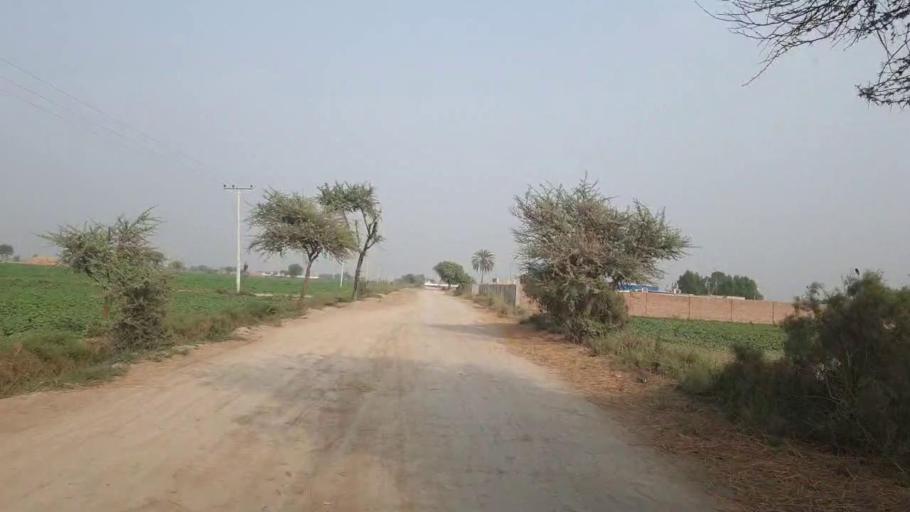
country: PK
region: Sindh
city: Mirpur Batoro
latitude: 24.5672
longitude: 68.4038
